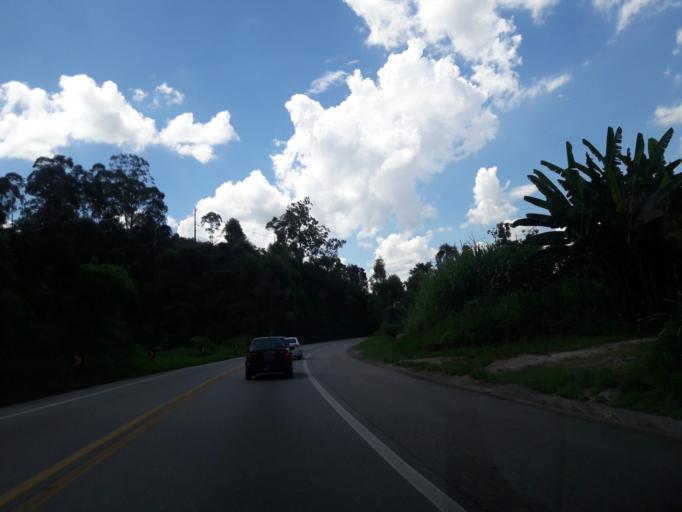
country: BR
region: Sao Paulo
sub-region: Cajamar
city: Cajamar
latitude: -23.3238
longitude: -46.8266
